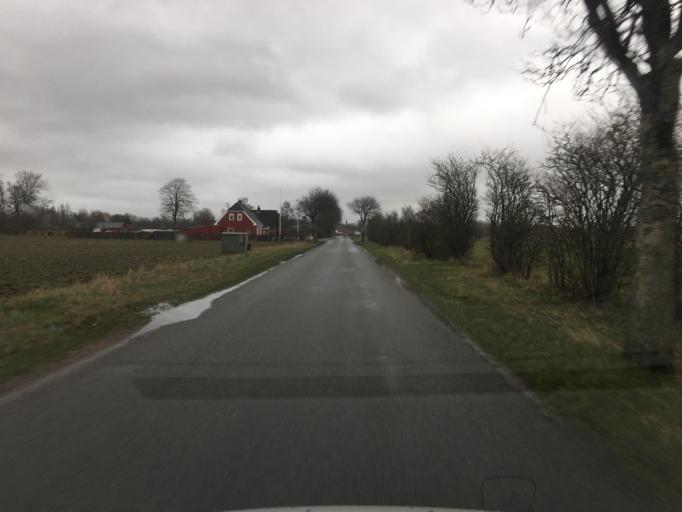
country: DK
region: South Denmark
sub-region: Aabenraa Kommune
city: Tinglev
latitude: 54.9040
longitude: 9.2638
